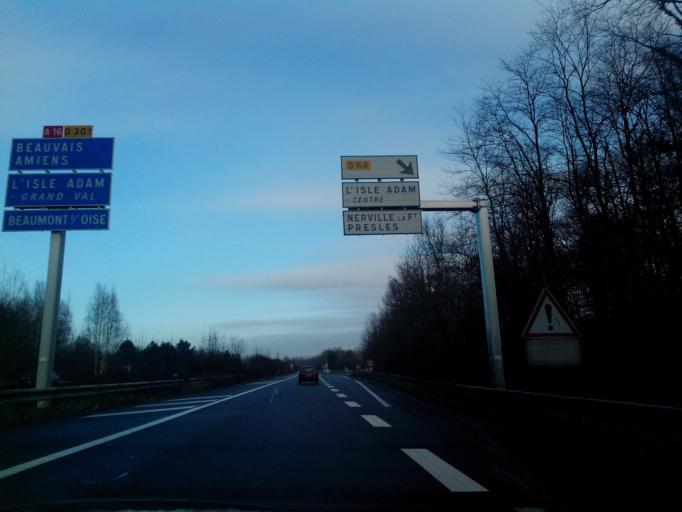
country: FR
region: Ile-de-France
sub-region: Departement du Val-d'Oise
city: Mours
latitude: 49.0970
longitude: 2.2627
